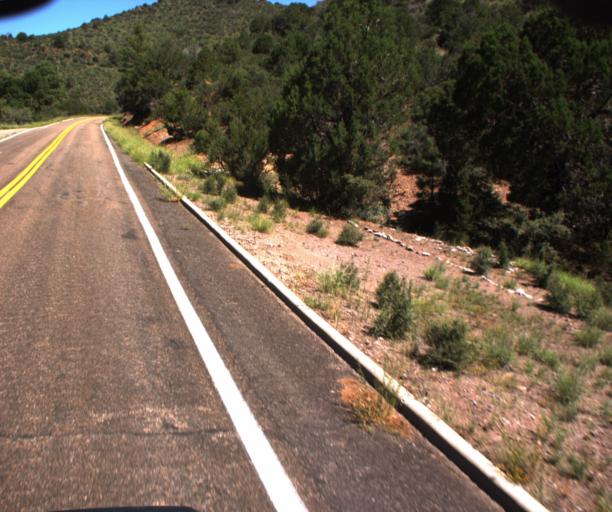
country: US
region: Arizona
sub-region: Greenlee County
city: Morenci
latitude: 33.2109
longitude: -109.3761
